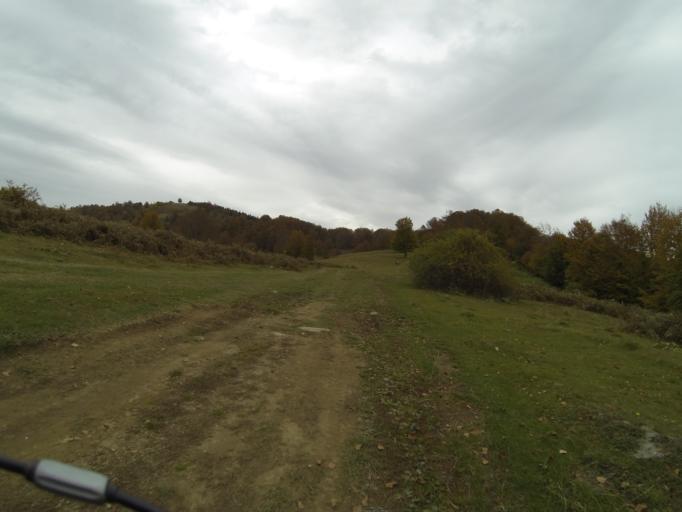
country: RO
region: Gorj
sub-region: Comuna Tismana
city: Sohodol
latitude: 45.1320
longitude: 22.8735
